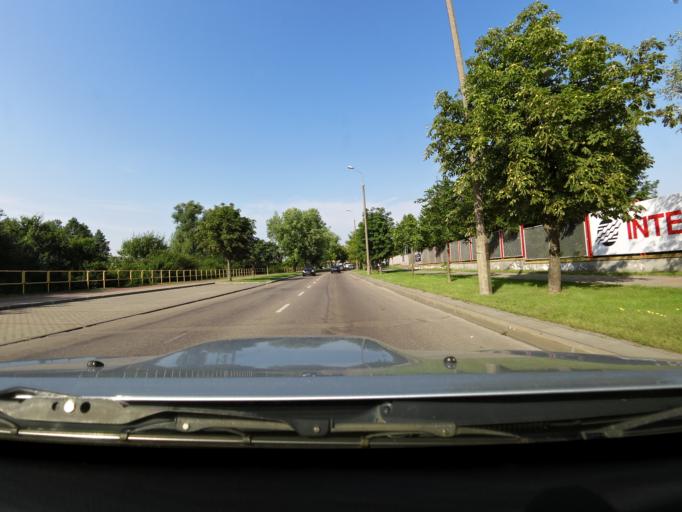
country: PL
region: Podlasie
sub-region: Suwalki
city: Suwalki
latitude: 54.0986
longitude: 22.9479
